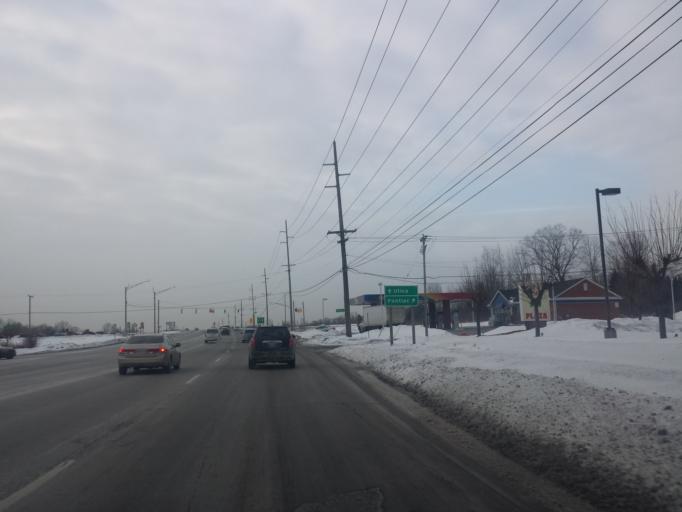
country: US
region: Michigan
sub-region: Oakland County
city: Troy
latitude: 42.6318
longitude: -83.1317
